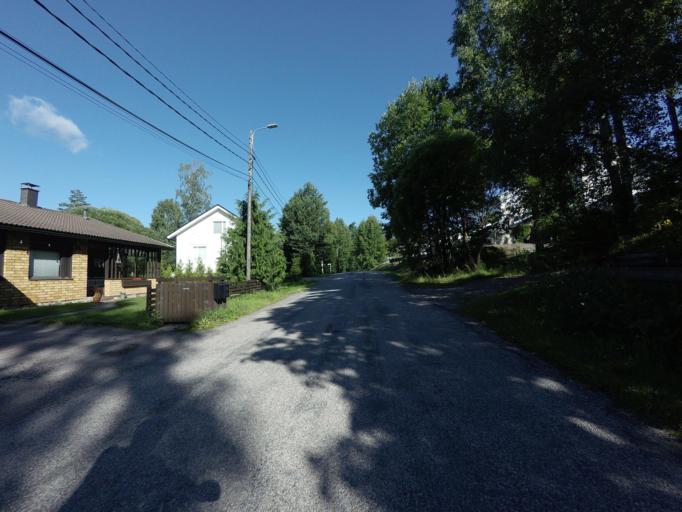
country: FI
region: Uusimaa
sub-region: Helsinki
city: Espoo
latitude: 60.1455
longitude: 24.6759
